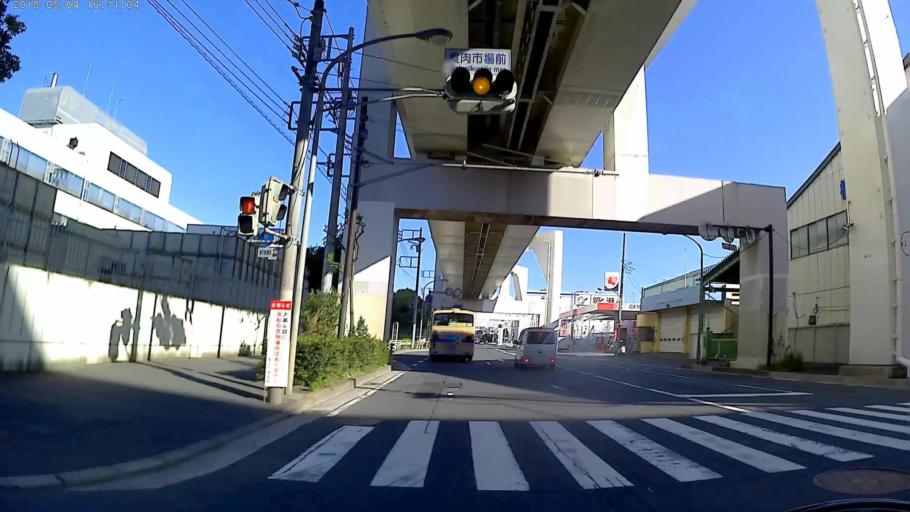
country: JP
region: Kanagawa
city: Yokohama
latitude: 35.4885
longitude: 139.6729
